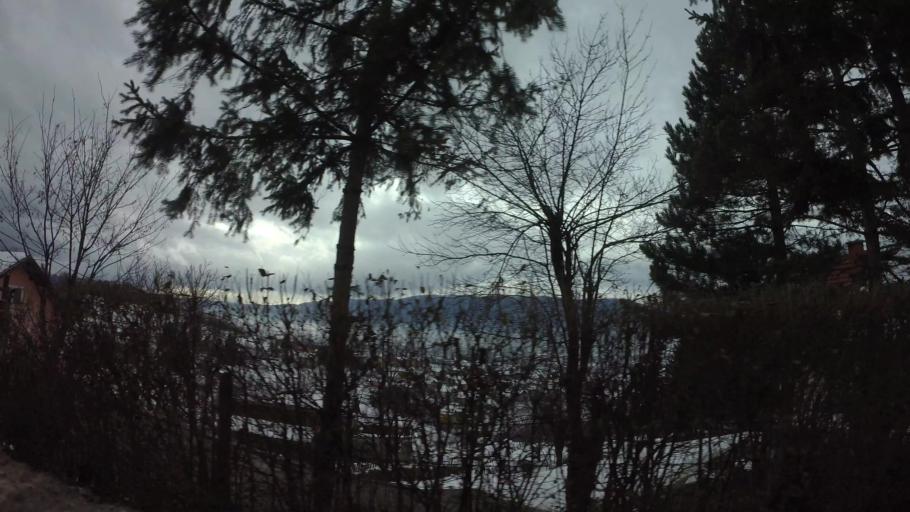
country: BA
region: Federation of Bosnia and Herzegovina
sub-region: Kanton Sarajevo
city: Sarajevo
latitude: 43.8621
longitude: 18.3364
